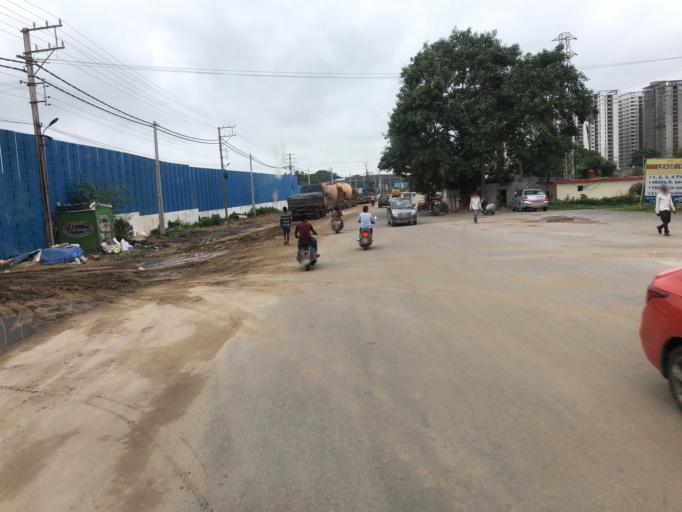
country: IN
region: Telangana
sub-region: Medak
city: Serilingampalle
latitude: 17.4663
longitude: 78.3384
